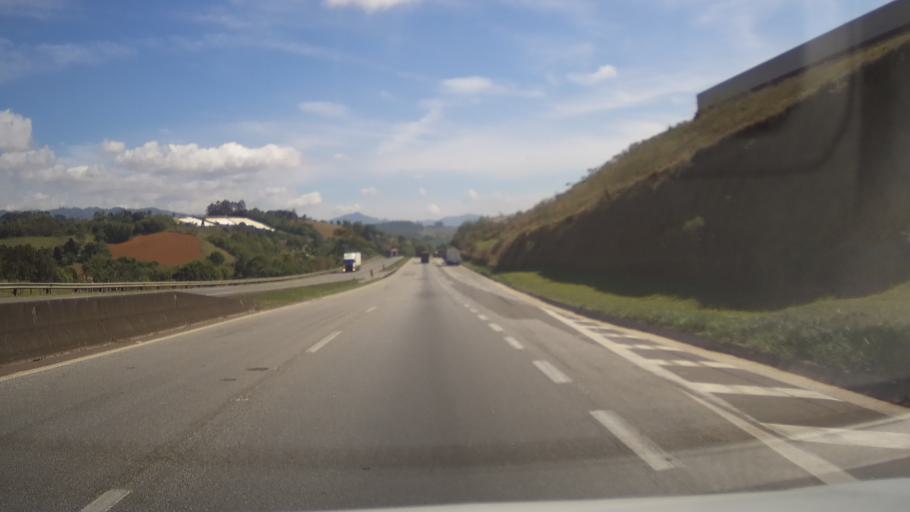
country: BR
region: Minas Gerais
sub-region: Cambui
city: Cambui
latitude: -22.5636
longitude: -46.0409
